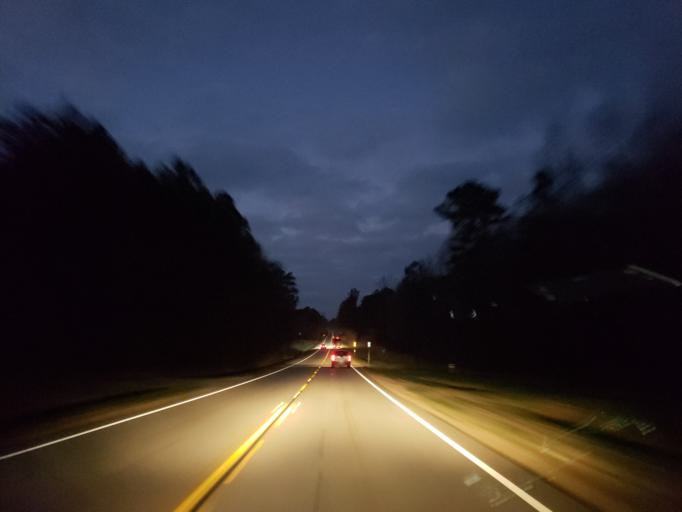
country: US
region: Georgia
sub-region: Polk County
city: Rockmart
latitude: 33.9303
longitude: -84.9968
